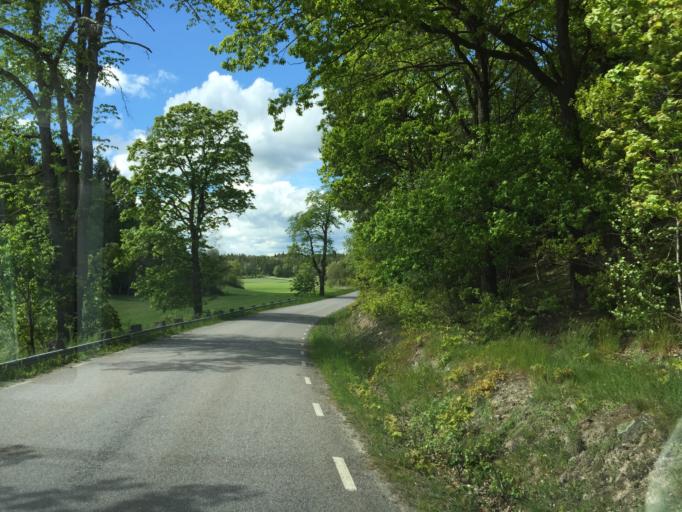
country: SE
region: OEstergoetland
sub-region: Norrkopings Kommun
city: Kimstad
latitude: 58.5157
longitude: 15.9634
